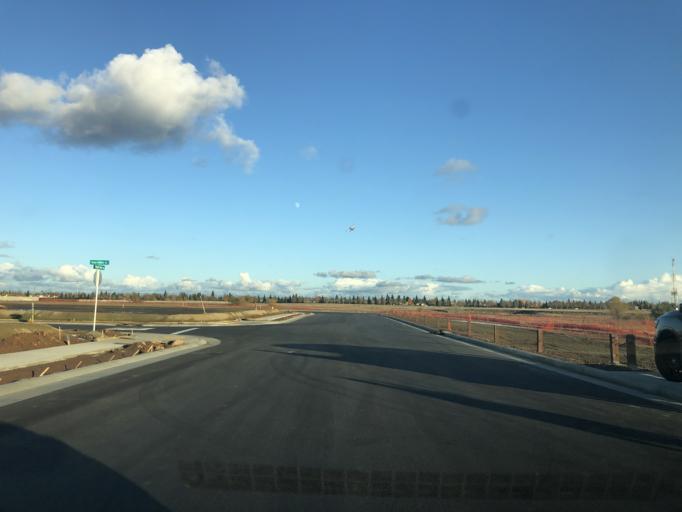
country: US
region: California
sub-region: Sacramento County
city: Antelope
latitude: 38.7561
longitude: -121.3676
